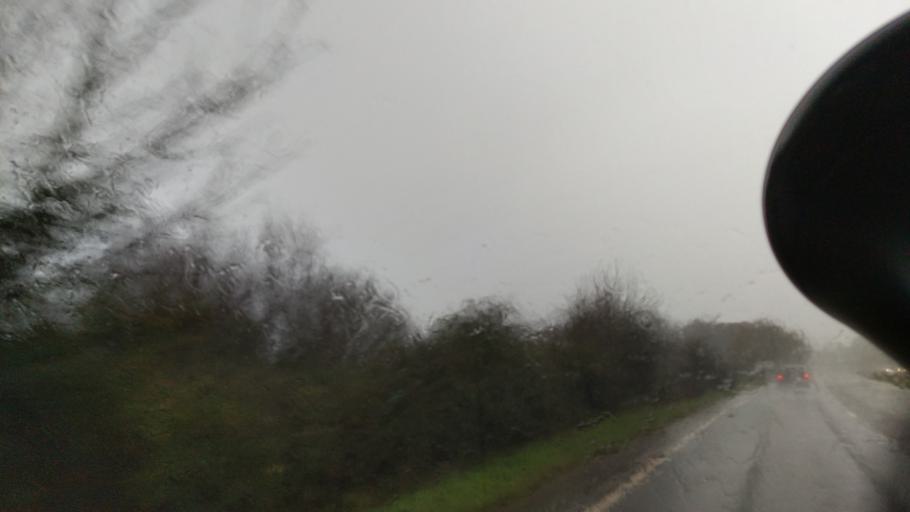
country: GB
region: England
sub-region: West Sussex
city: Walberton
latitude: 50.8530
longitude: -0.6270
